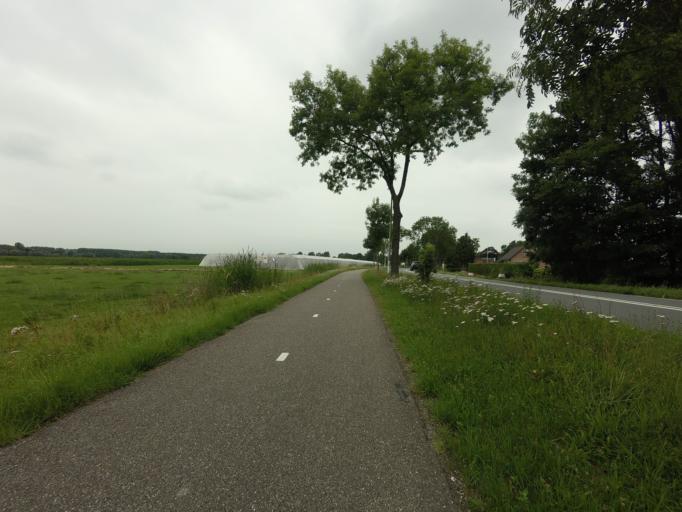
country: NL
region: Utrecht
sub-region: Stichtse Vecht
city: Spechtenkamp
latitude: 52.1586
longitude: 5.0157
